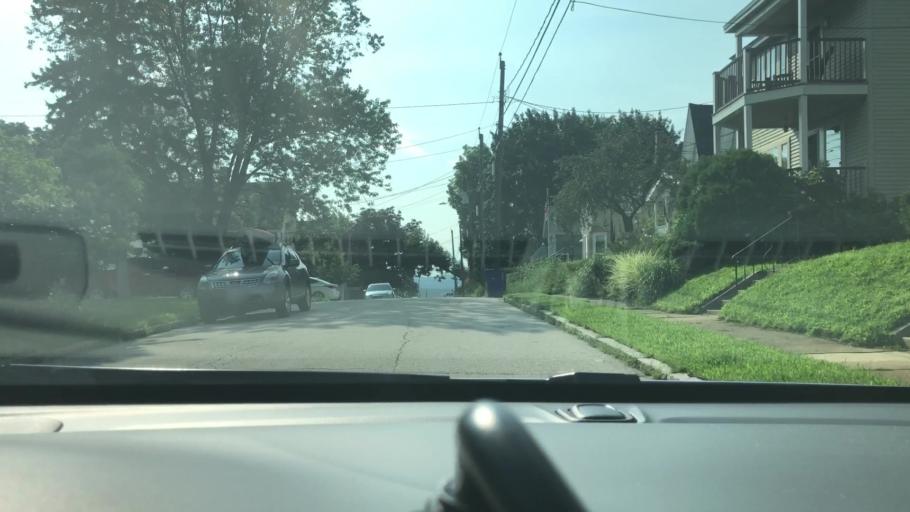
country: US
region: New Hampshire
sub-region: Hillsborough County
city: Manchester
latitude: 42.9894
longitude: -71.4413
